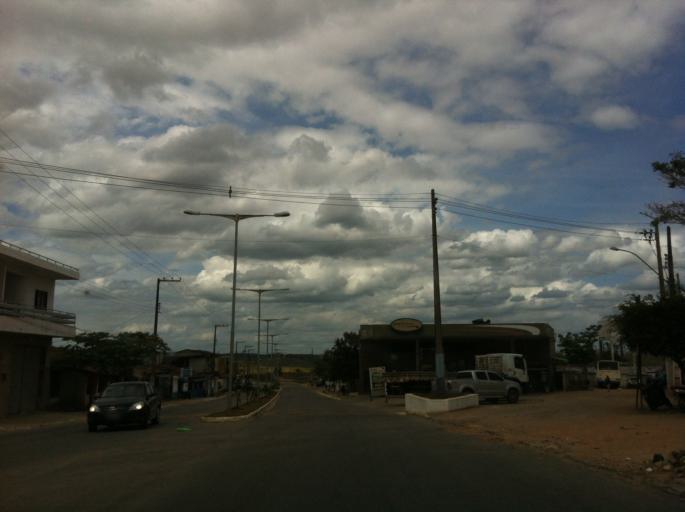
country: BR
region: Alagoas
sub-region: Ibateguara
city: Ibateguara
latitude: -8.9678
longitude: -35.9230
